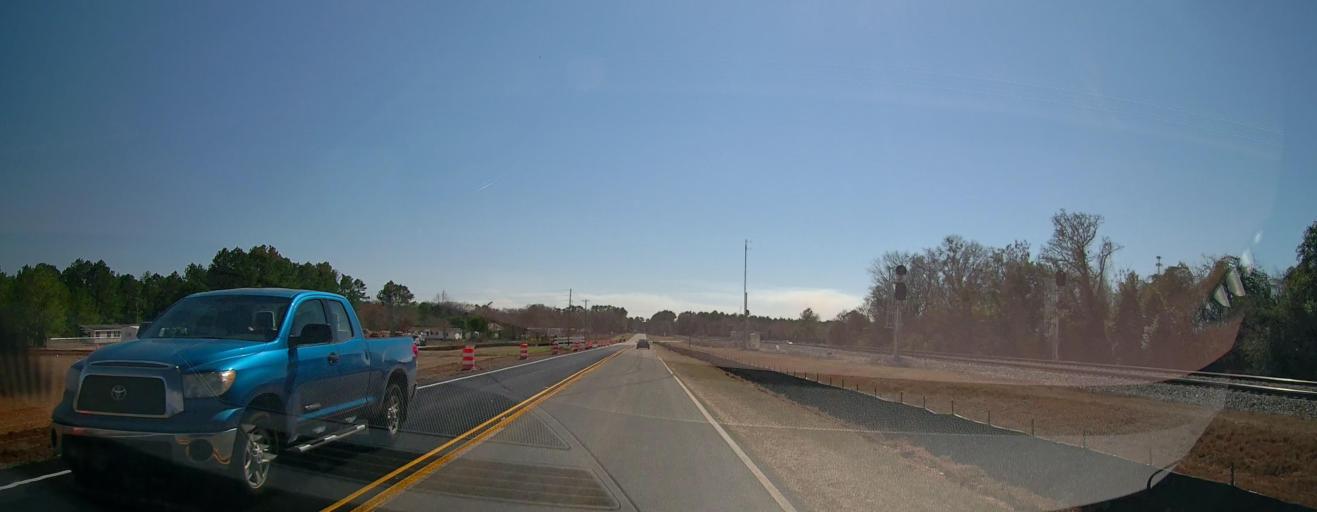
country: US
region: Georgia
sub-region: Houston County
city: Perry
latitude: 32.4668
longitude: -83.6173
